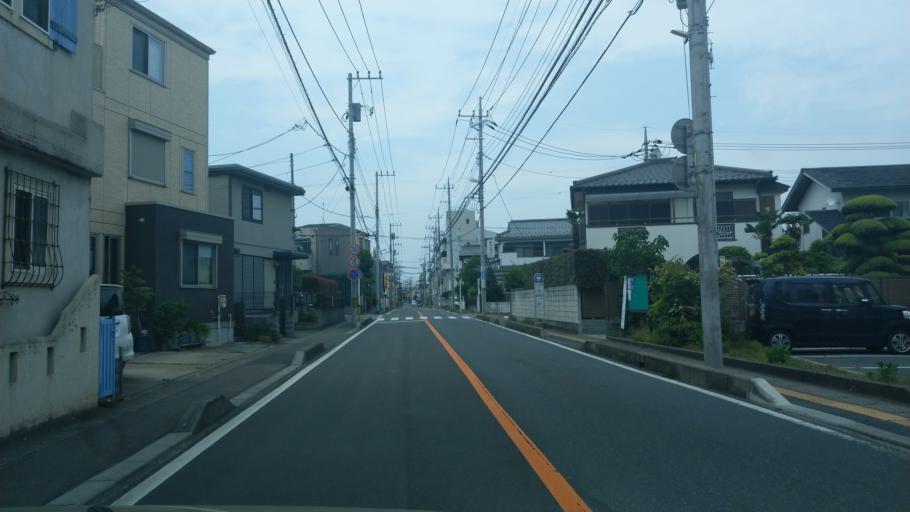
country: JP
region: Saitama
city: Yono
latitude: 35.9095
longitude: 139.6096
